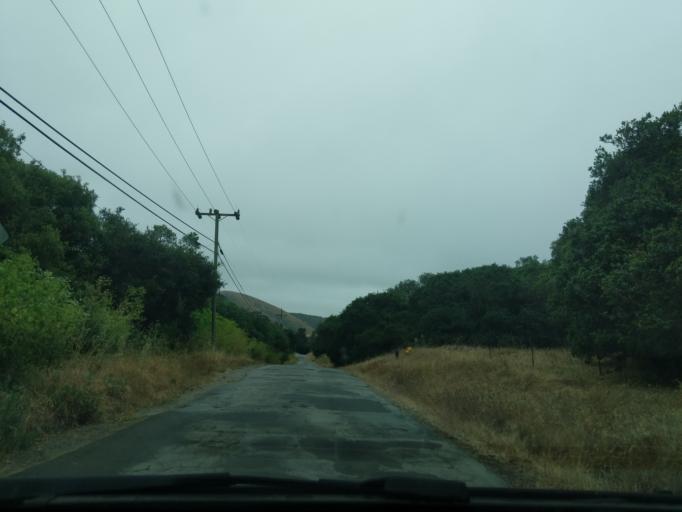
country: US
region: California
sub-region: San Benito County
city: Aromas
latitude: 36.8737
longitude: -121.6213
